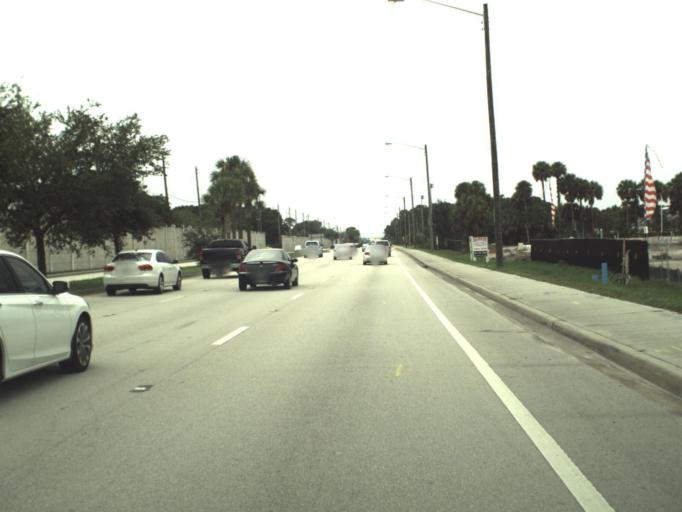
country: US
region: Florida
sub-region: Palm Beach County
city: Schall Circle
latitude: 26.7302
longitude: -80.1103
